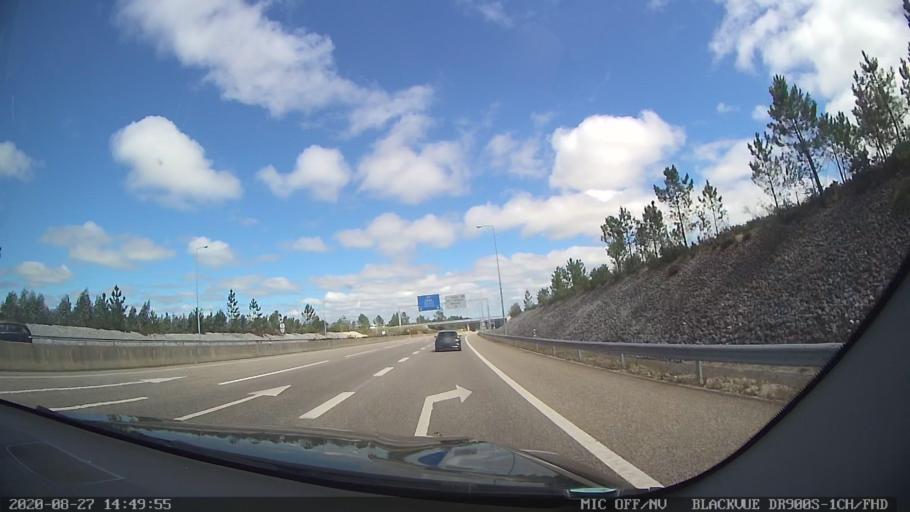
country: PT
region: Leiria
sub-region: Marinha Grande
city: Marinha Grande
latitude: 39.7424
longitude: -8.8756
